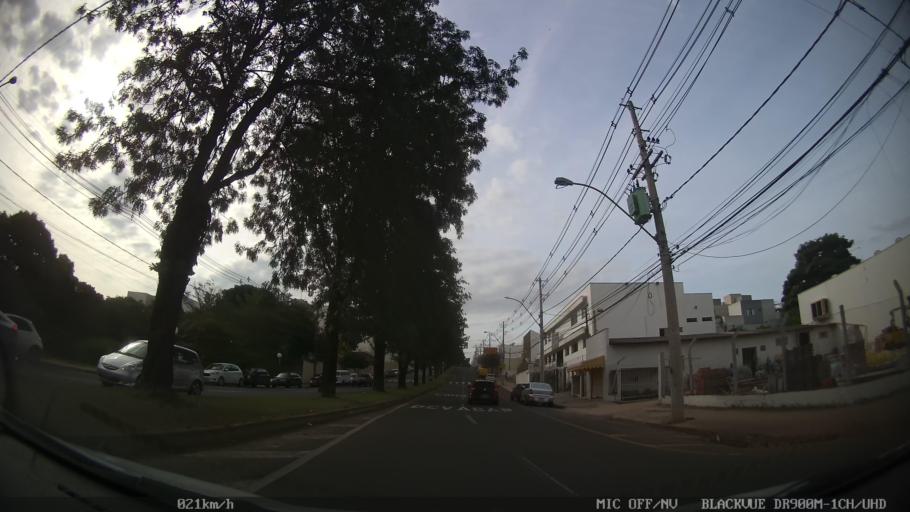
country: BR
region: Sao Paulo
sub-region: Piracicaba
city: Piracicaba
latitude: -22.7323
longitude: -47.6219
